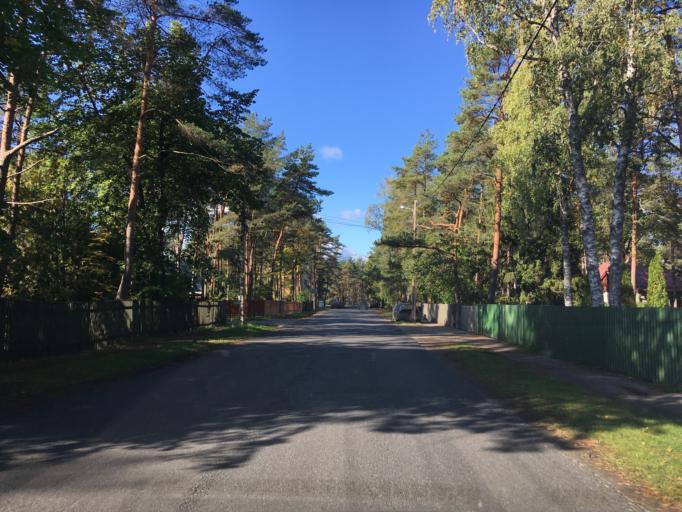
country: EE
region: Harju
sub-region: Saue vald
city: Laagri
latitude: 59.3752
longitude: 24.6822
